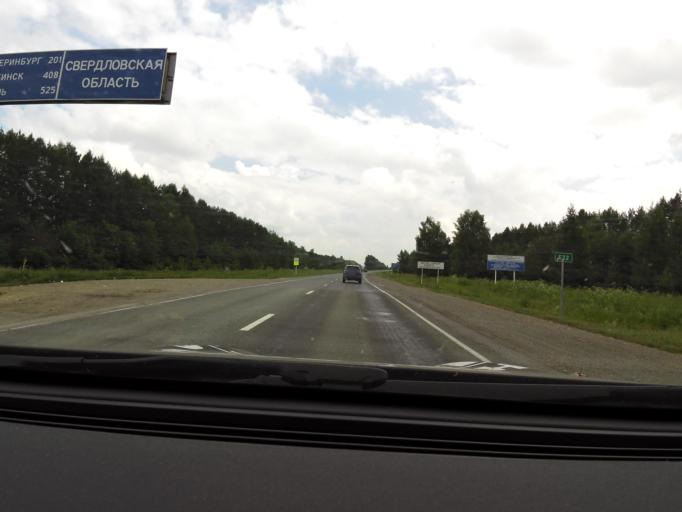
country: RU
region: Perm
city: Suksun
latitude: 56.9122
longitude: 57.5857
